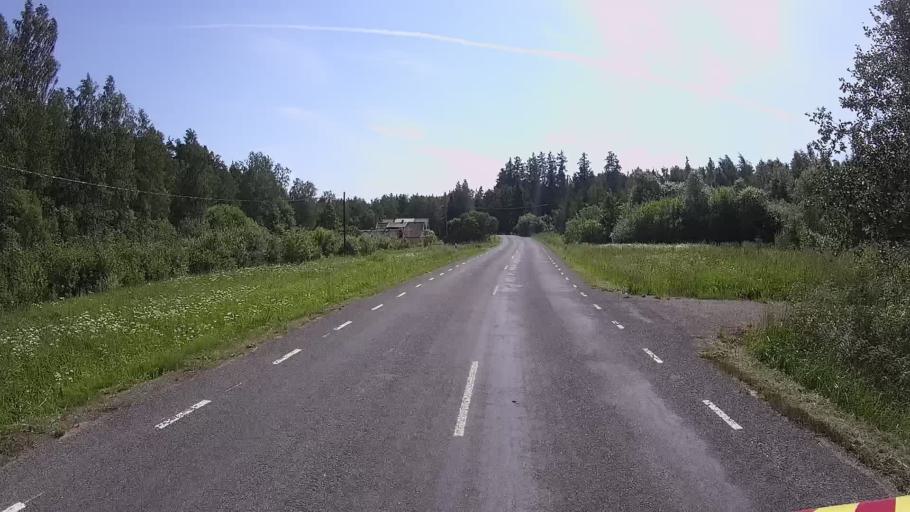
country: EE
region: Viljandimaa
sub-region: Karksi vald
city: Karksi-Nuia
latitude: 58.0877
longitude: 25.5585
